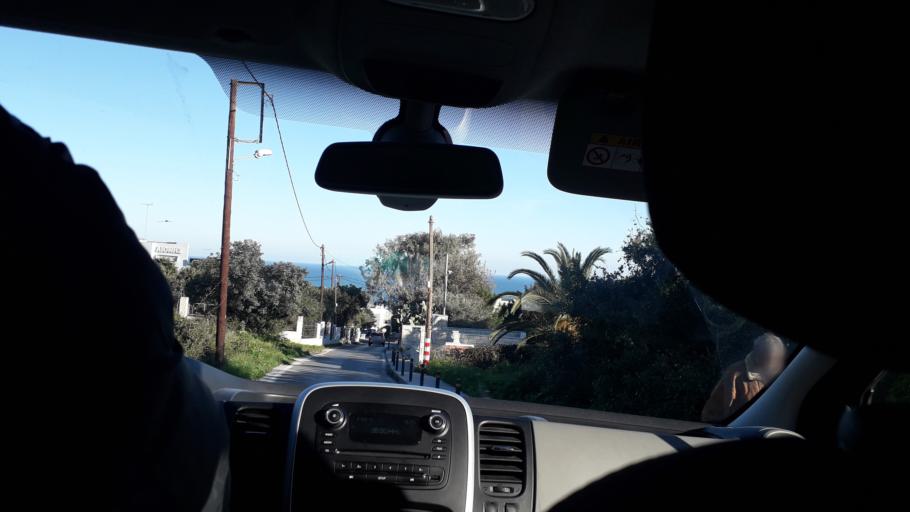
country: GR
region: Crete
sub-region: Nomos Rethymnis
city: Atsipopoulon
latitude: 35.3606
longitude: 24.4423
